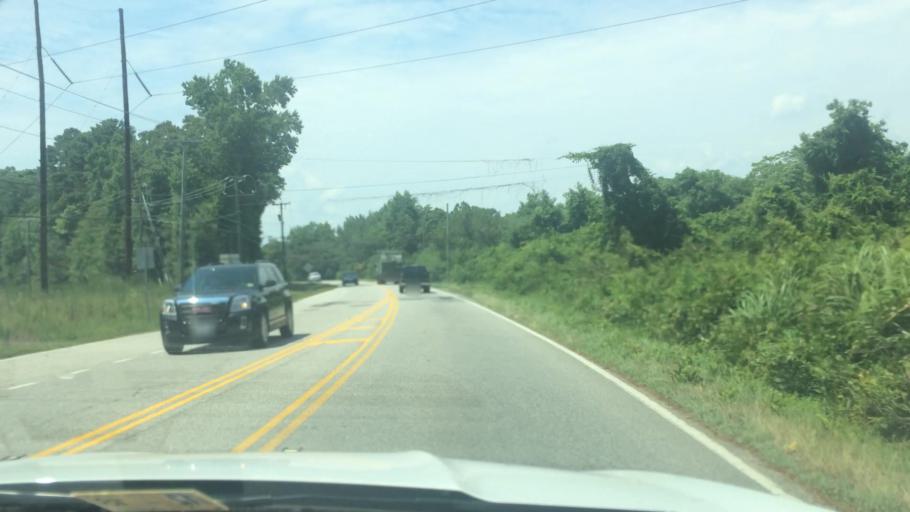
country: US
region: Virginia
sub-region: City of Williamsburg
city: Williamsburg
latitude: 37.2319
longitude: -76.6275
